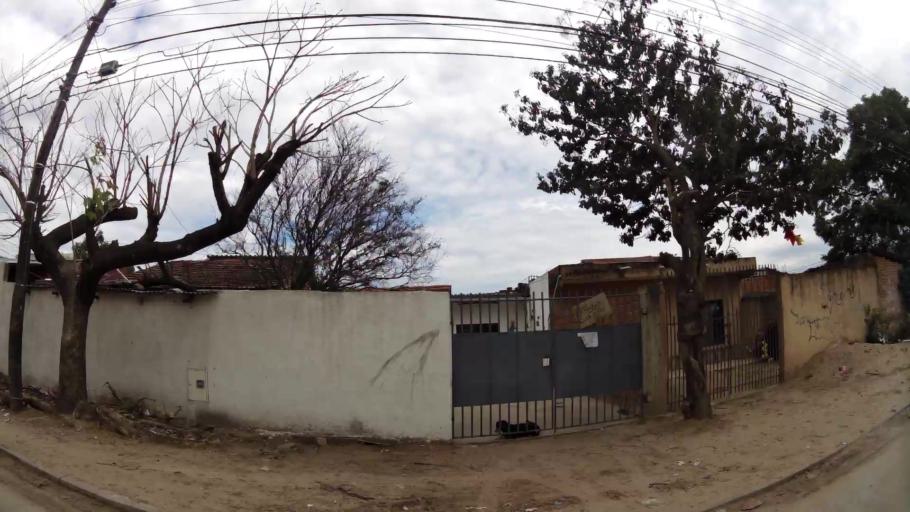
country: BO
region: Santa Cruz
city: Santa Cruz de la Sierra
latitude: -17.7385
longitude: -63.1915
